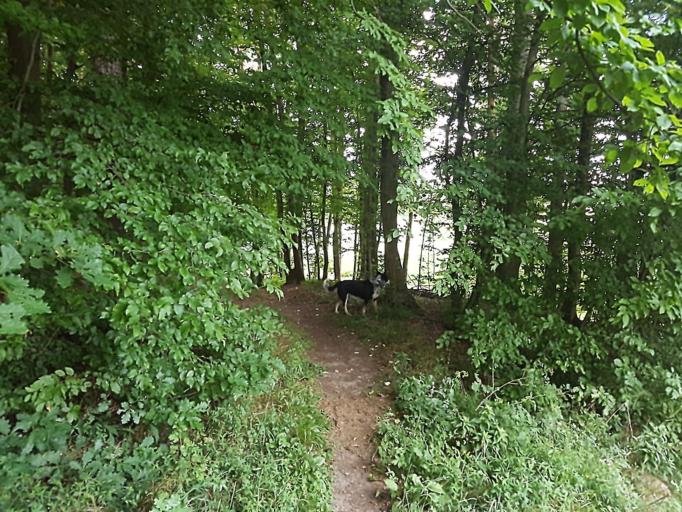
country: DE
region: Bavaria
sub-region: Upper Franconia
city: Litzendorf
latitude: 49.9249
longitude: 10.9918
